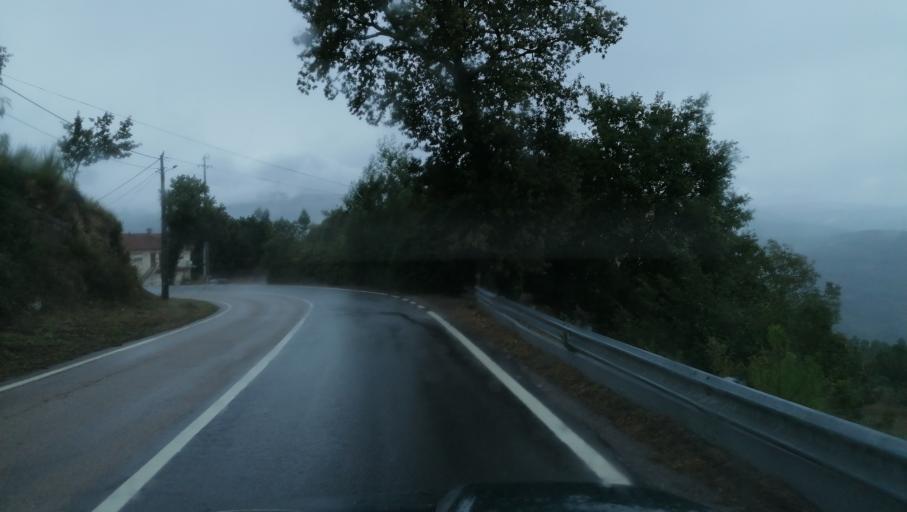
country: PT
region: Vila Real
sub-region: Ribeira de Pena
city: Ribeira de Pena
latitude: 41.5210
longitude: -7.8102
